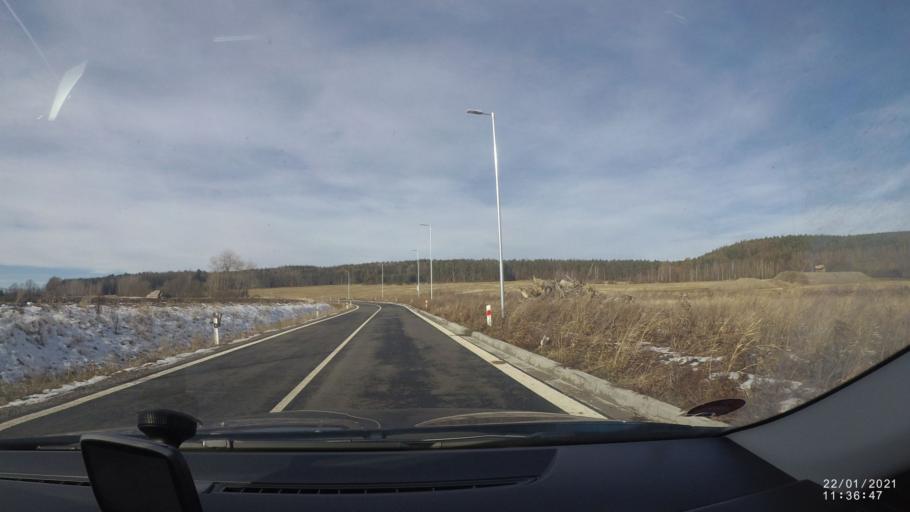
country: CZ
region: Plzensky
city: Zbiroh
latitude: 49.8415
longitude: 13.8106
